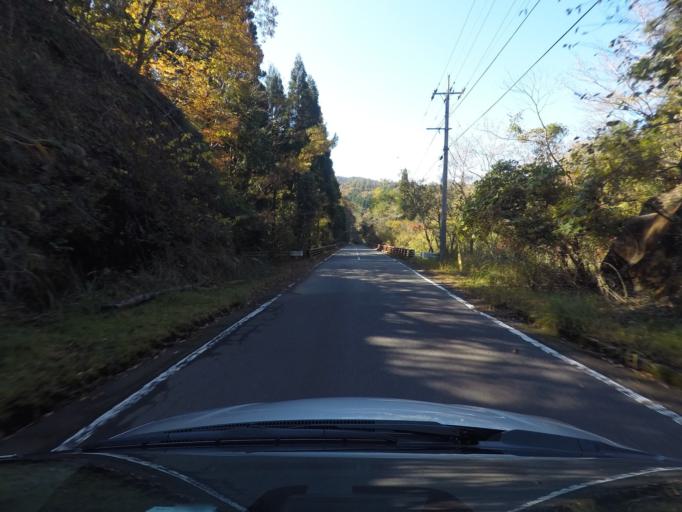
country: JP
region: Miyazaki
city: Kobayashi
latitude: 32.0590
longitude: 131.0875
